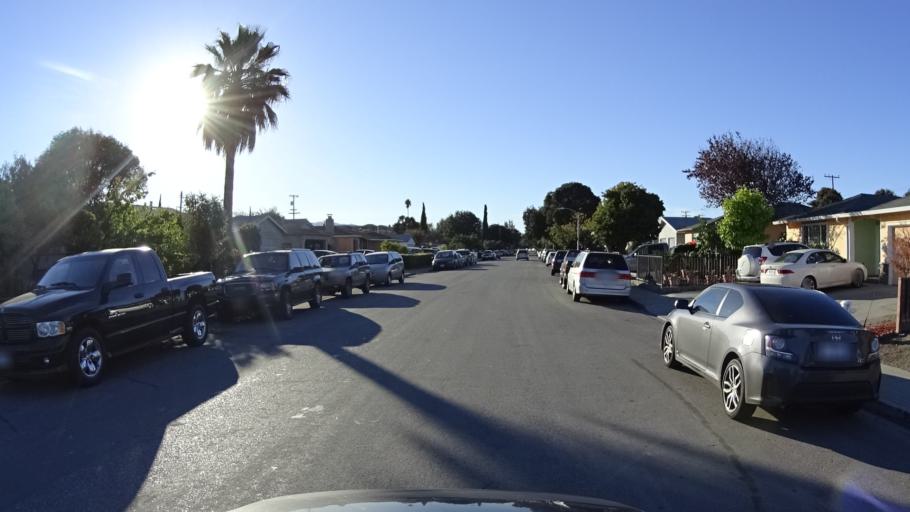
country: US
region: California
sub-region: Santa Clara County
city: Santa Clara
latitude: 37.3699
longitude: -121.9879
